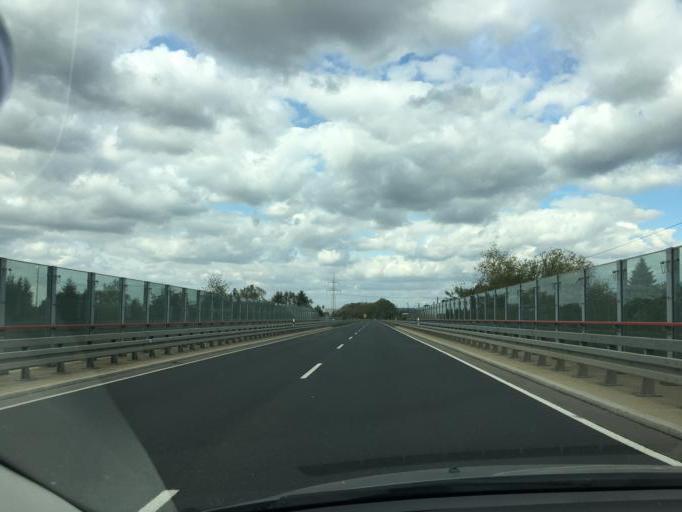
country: DE
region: Saxony
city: Coswig
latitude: 51.0985
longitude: 13.6039
